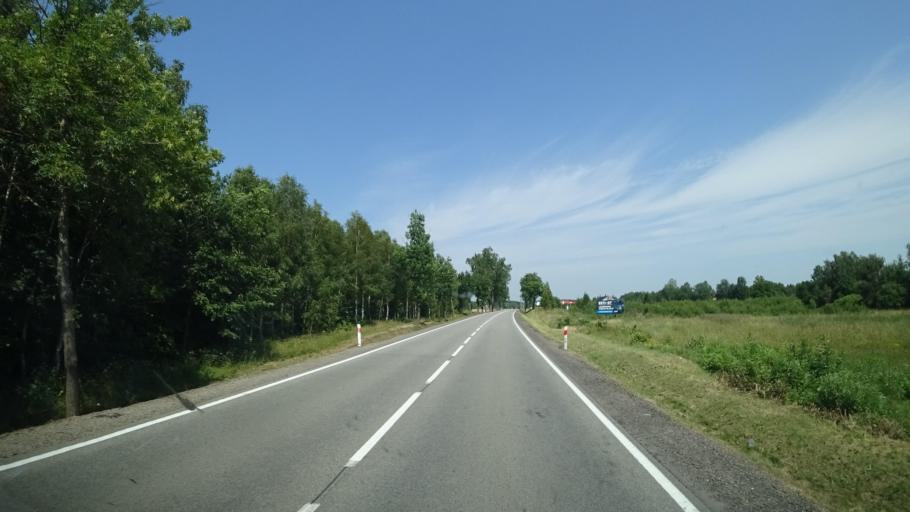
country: PL
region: Pomeranian Voivodeship
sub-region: Powiat koscierski
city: Koscierzyna
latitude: 54.1564
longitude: 18.0330
